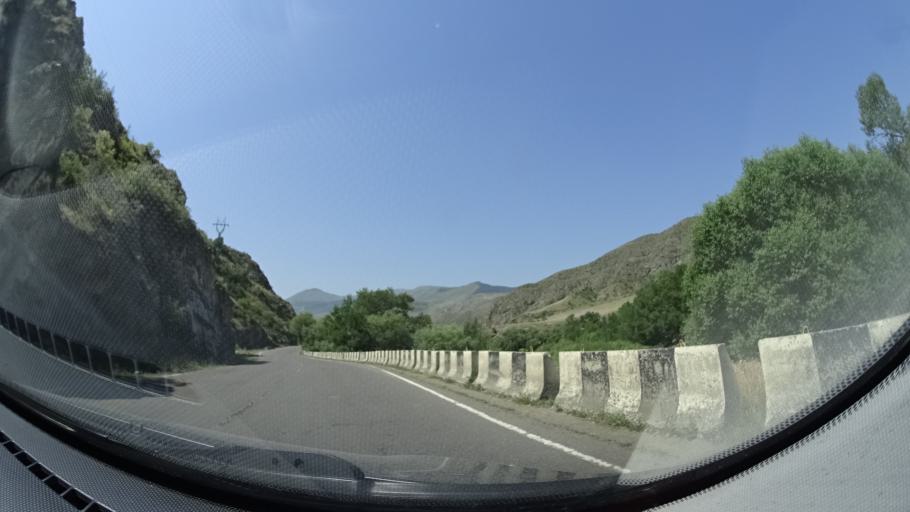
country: GE
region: Samtskhe-Javakheti
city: Aspindza
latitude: 41.5576
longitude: 43.2712
